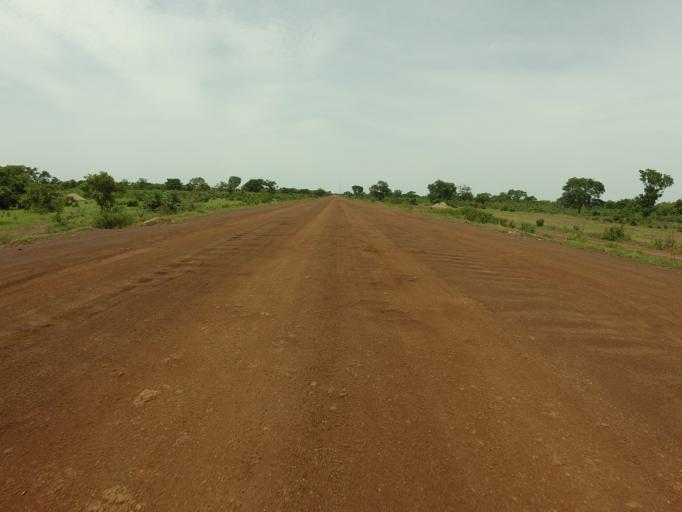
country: GH
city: Kpandae
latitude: 8.8859
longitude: 0.0289
